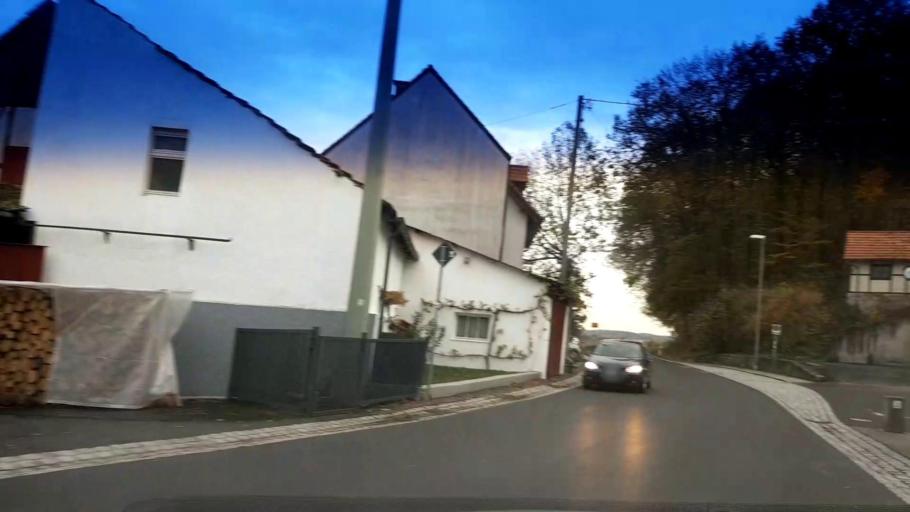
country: DE
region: Bavaria
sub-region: Regierungsbezirk Unterfranken
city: Stettfeld
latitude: 49.9573
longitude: 10.7134
